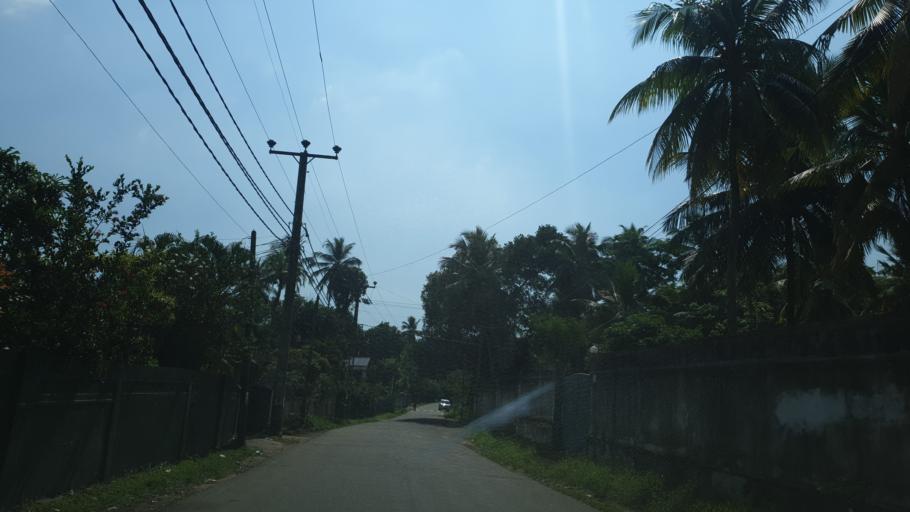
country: LK
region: Western
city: Moratuwa
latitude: 6.7652
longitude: 79.9306
